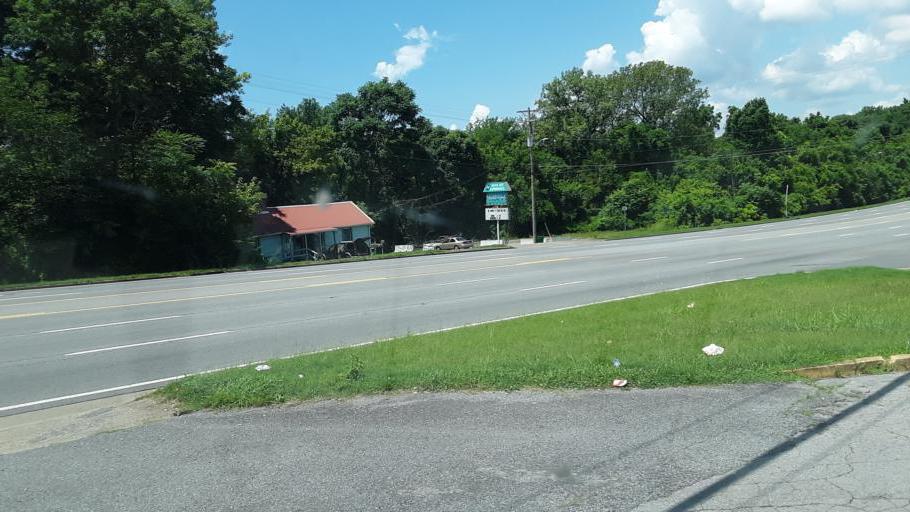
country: US
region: Kentucky
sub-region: Christian County
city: Fort Campbell North
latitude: 36.6067
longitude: -87.4259
